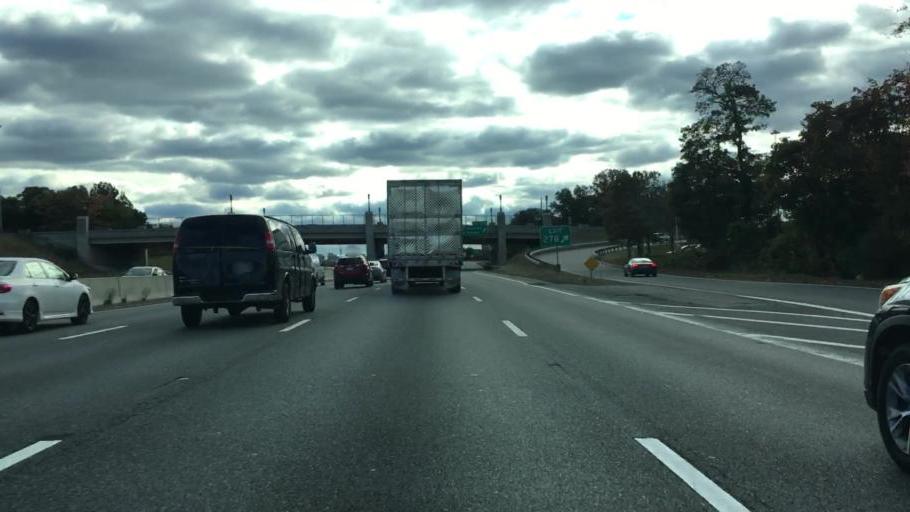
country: US
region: Massachusetts
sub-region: Middlesex County
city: Waltham
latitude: 42.3987
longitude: -71.2608
